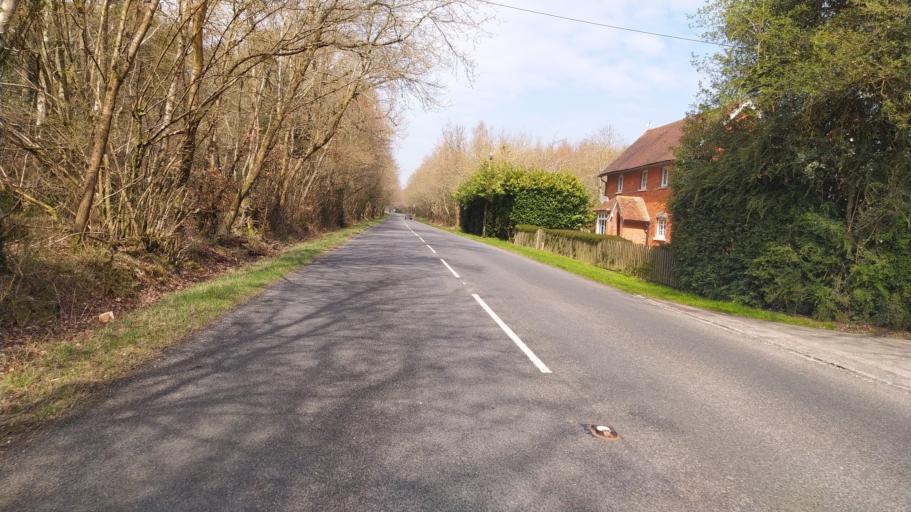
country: GB
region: England
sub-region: West Berkshire
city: Welford
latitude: 51.4190
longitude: -1.3863
